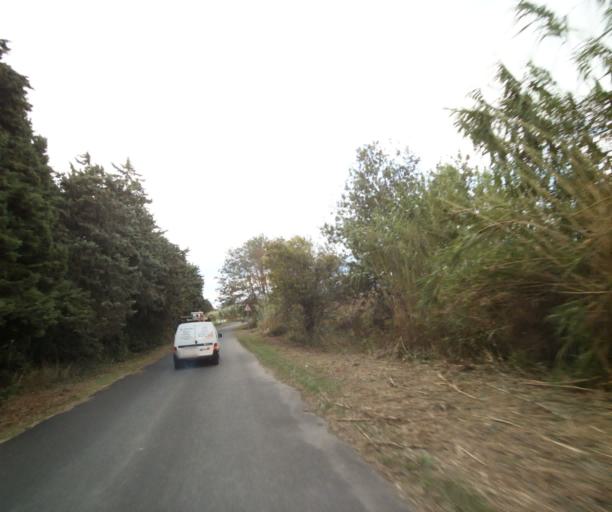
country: FR
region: Languedoc-Roussillon
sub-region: Departement des Pyrenees-Orientales
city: Latour-Bas-Elne
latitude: 42.5844
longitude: 3.0314
